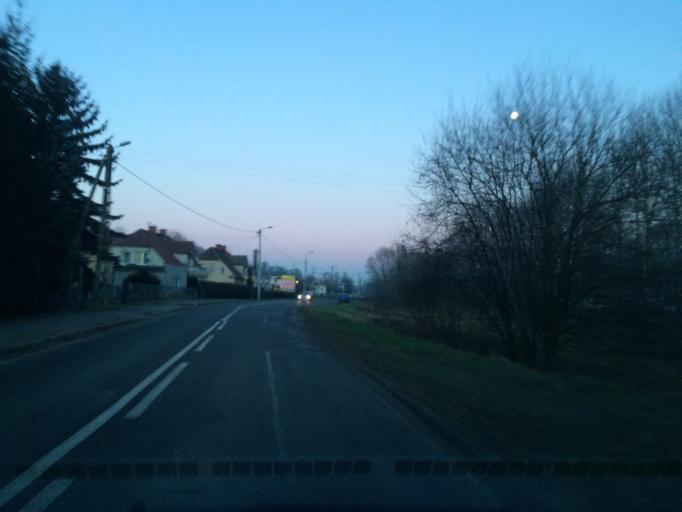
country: PL
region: Lower Silesian Voivodeship
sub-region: Powiat zlotoryjski
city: Zlotoryja
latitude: 51.1276
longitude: 15.9064
